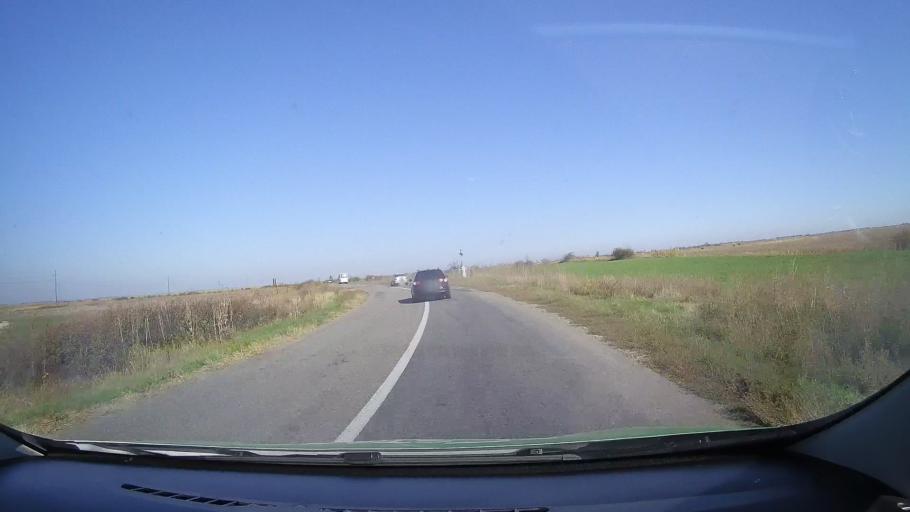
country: RO
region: Satu Mare
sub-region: Comuna Cauas
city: Cauas
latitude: 47.5758
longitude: 22.5501
